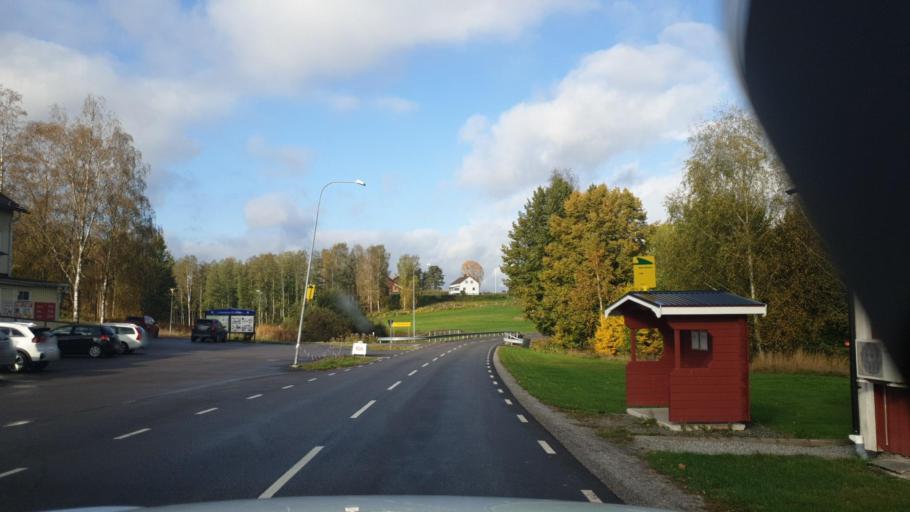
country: SE
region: Vaermland
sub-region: Arvika Kommun
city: Arvika
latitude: 59.5484
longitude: 12.5646
